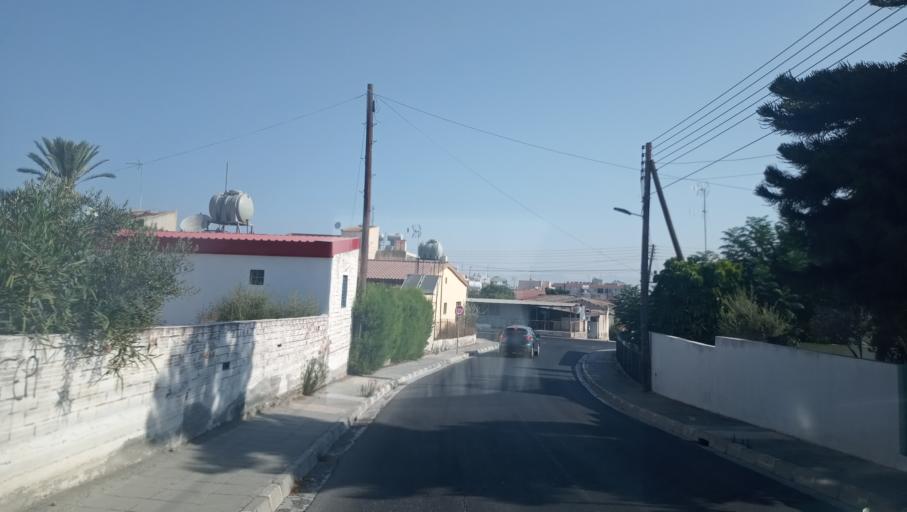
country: CY
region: Lefkosia
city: Geri
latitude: 35.1056
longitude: 33.4227
